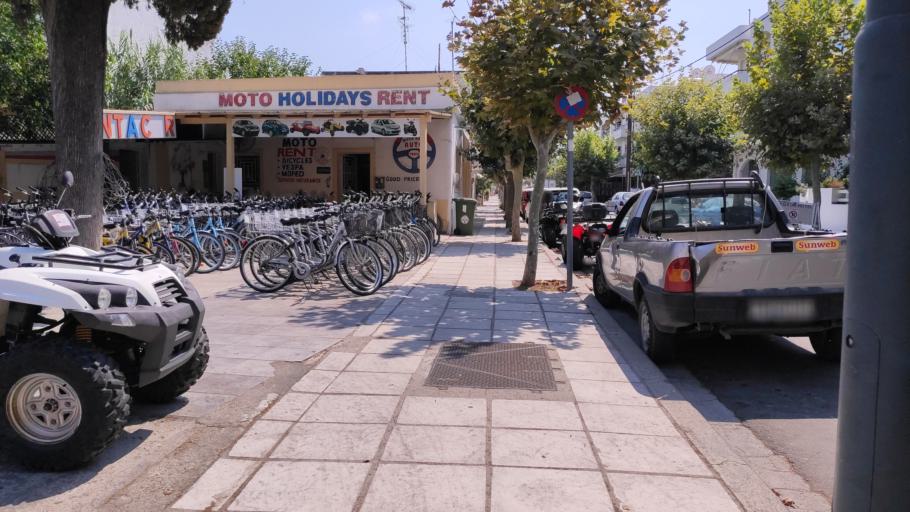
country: GR
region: South Aegean
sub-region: Nomos Dodekanisou
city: Kos
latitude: 36.8927
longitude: 27.2844
